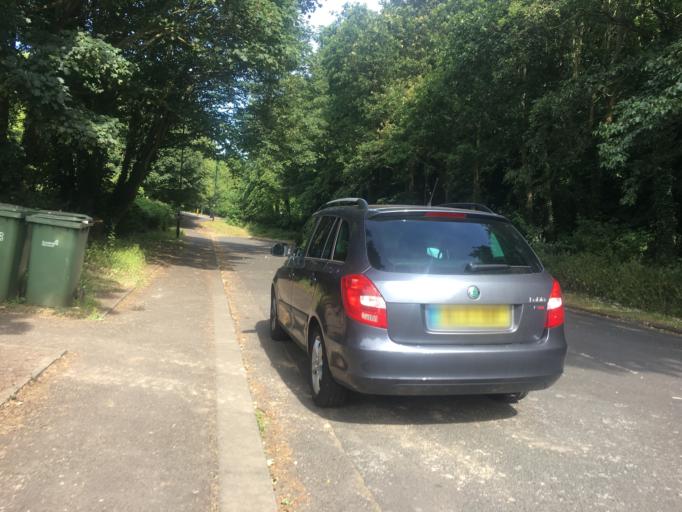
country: GB
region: England
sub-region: Sunderland
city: Washington
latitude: 54.8795
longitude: -1.5298
